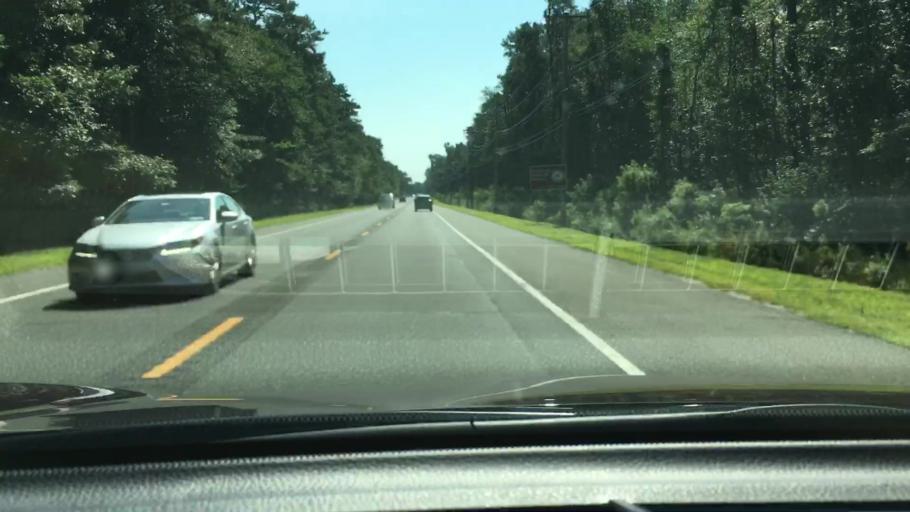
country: US
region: New Jersey
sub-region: Cumberland County
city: Laurel Lake
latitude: 39.3770
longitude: -74.9571
